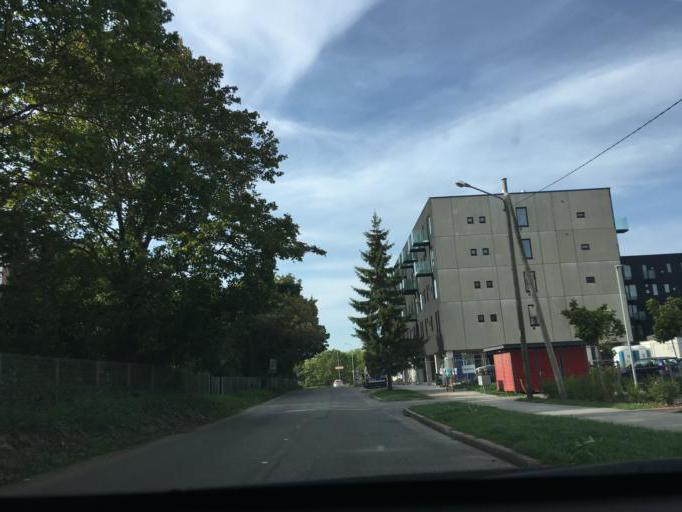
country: EE
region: Harju
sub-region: Tallinna linn
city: Tallinn
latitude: 59.4381
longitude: 24.8056
